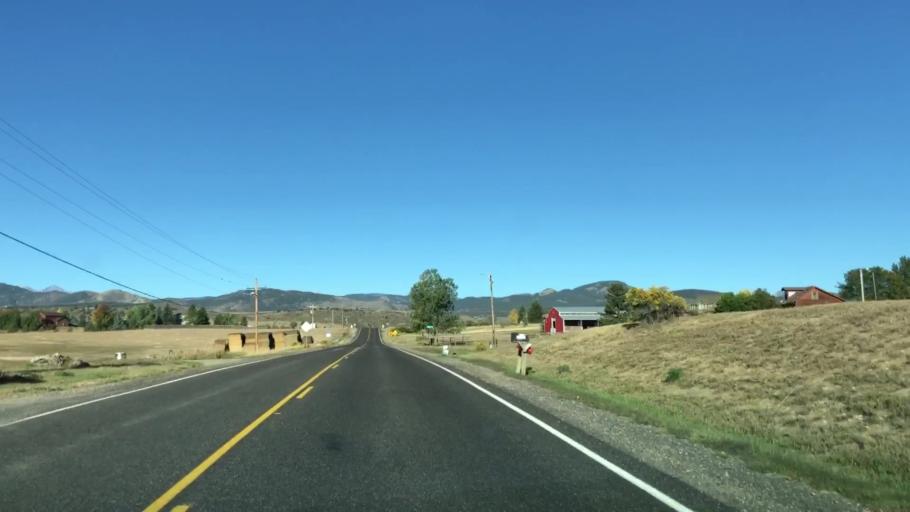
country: US
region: Colorado
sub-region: Larimer County
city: Loveland
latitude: 40.3785
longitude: -105.1587
